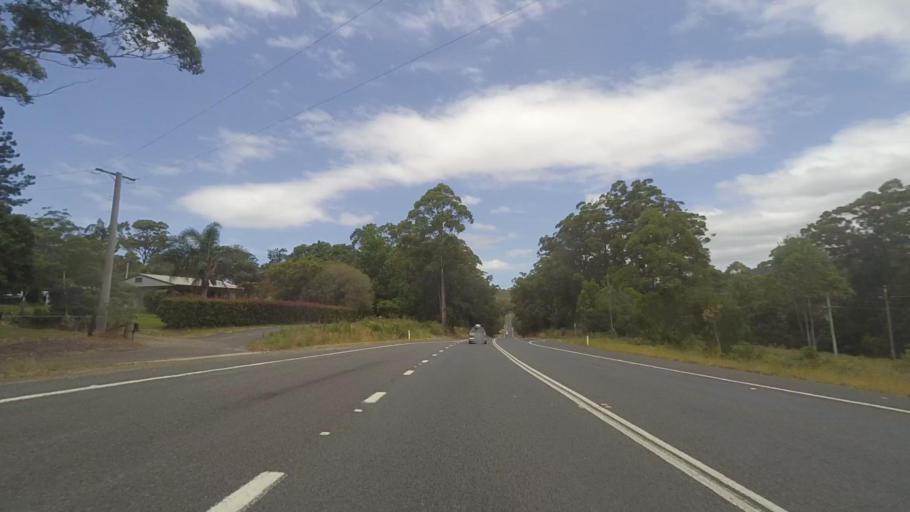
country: AU
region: New South Wales
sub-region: Shoalhaven Shire
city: Milton
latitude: -35.2232
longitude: 150.4360
